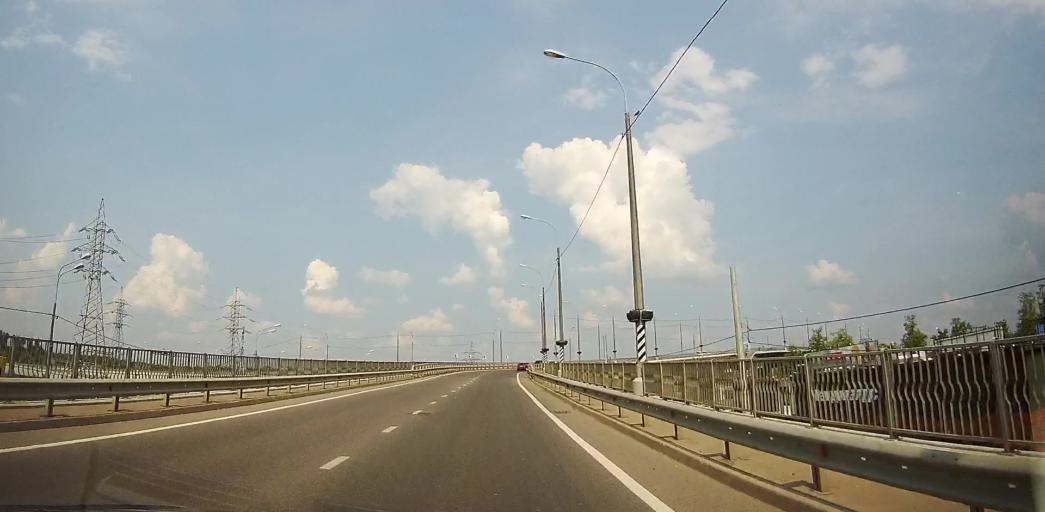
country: RU
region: Moskovskaya
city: Stupino
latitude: 54.9035
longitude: 38.0789
